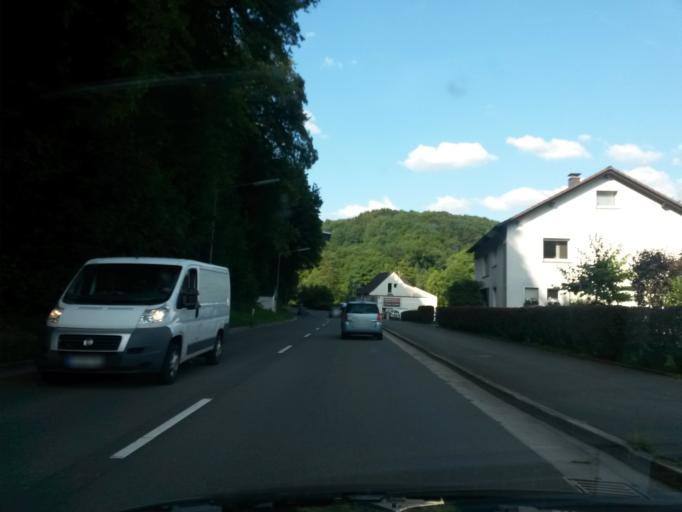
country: DE
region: North Rhine-Westphalia
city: Wiehl
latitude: 50.9723
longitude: 7.4876
